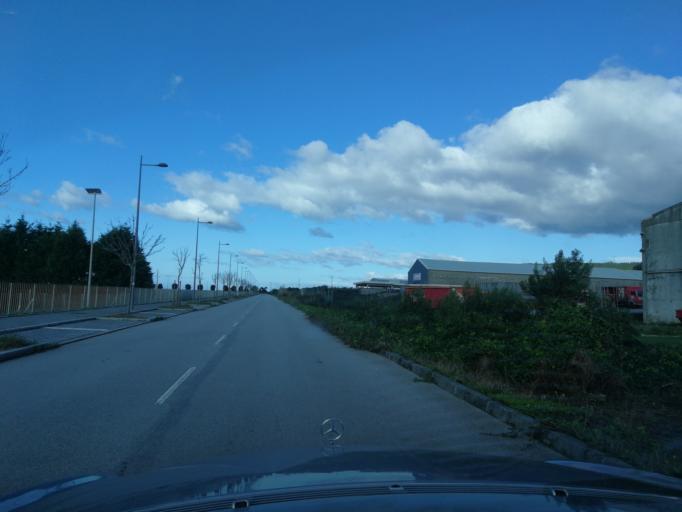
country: PT
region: Viana do Castelo
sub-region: Viana do Castelo
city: Viana do Castelo
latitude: 41.6961
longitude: -8.8466
